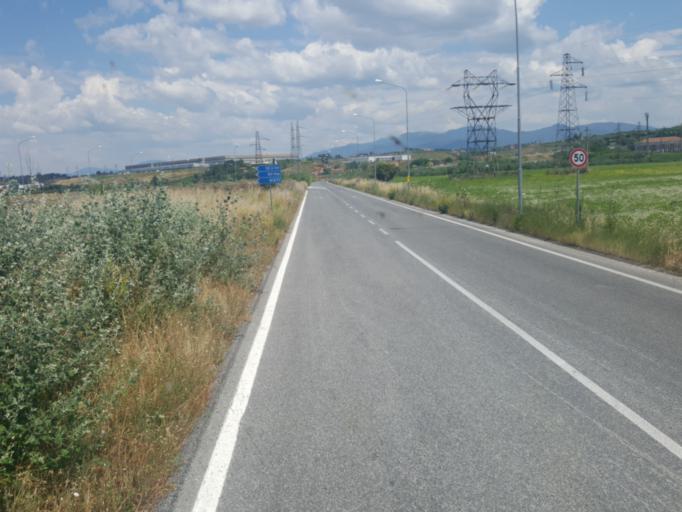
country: IT
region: Latium
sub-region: Citta metropolitana di Roma Capitale
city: Fiano Romano
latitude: 42.1569
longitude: 12.6430
